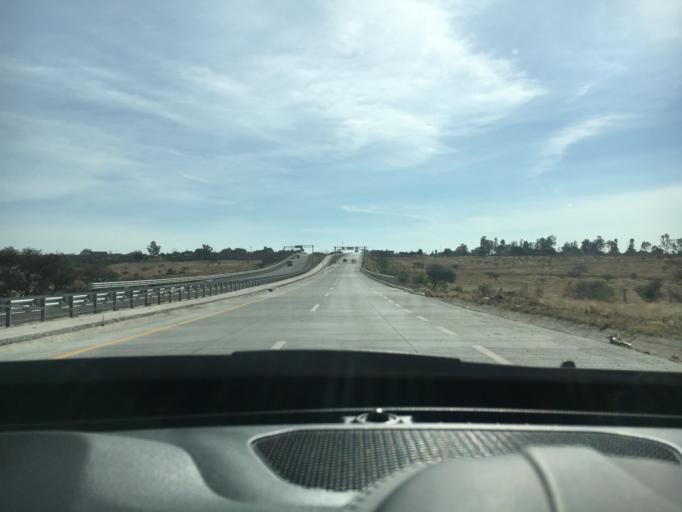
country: MX
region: Guanajuato
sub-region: Silao de la Victoria
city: El Refugio de los Sauces
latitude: 21.0462
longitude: -101.5245
